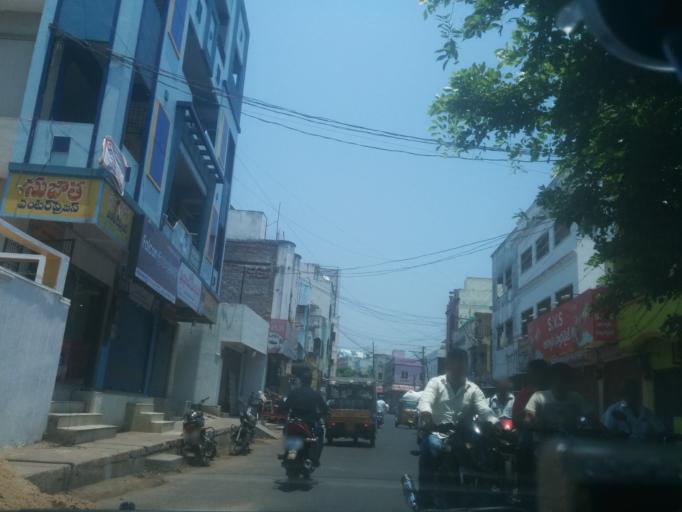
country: IN
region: Andhra Pradesh
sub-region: East Godavari
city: Rajahmundry
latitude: 16.9983
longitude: 81.7752
